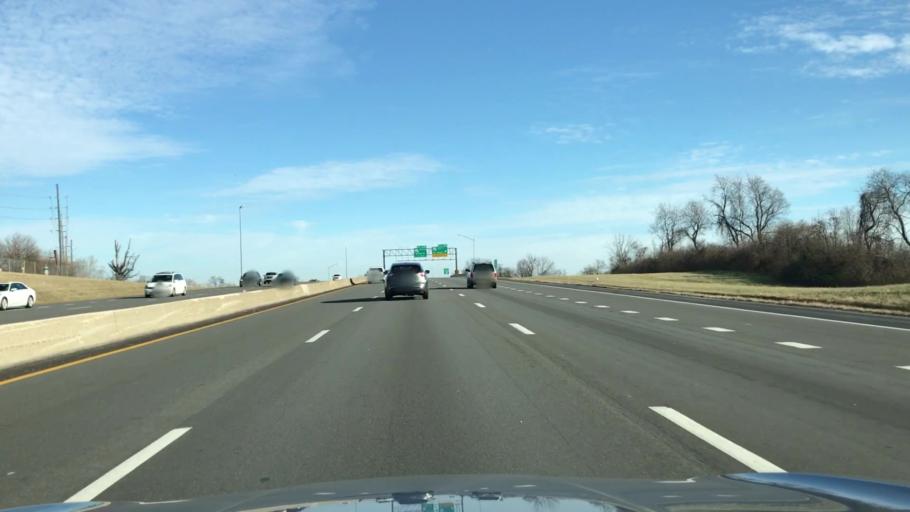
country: US
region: Missouri
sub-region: Saint Louis County
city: Castle Point
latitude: 38.7707
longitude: -90.2452
